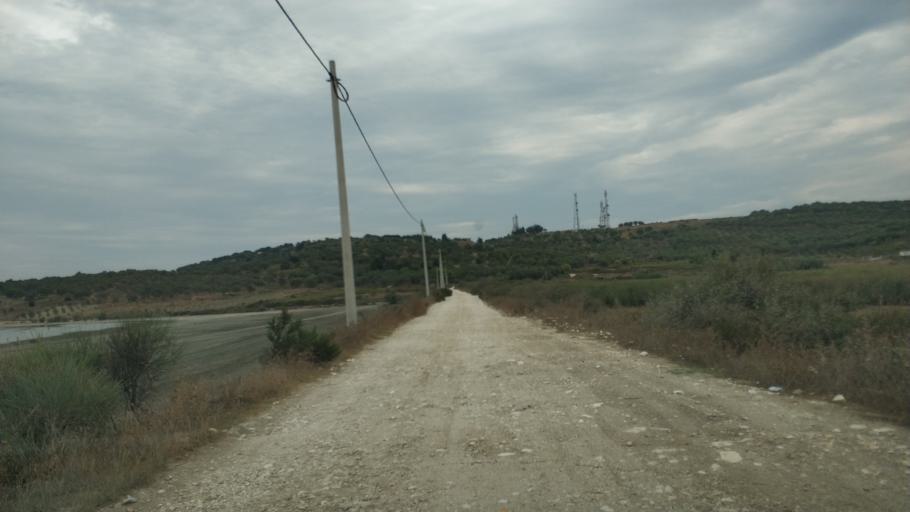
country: AL
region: Vlore
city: Vlore
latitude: 40.5113
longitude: 19.4055
